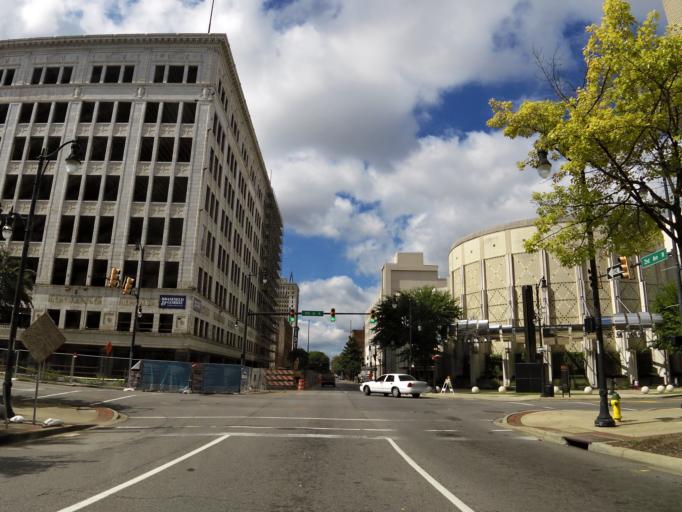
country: US
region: Alabama
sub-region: Jefferson County
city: Birmingham
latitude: 33.5148
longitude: -86.8074
